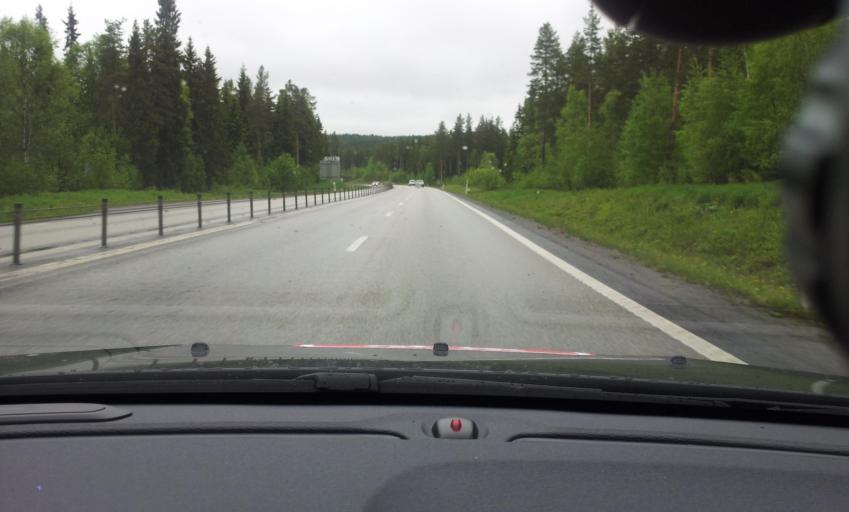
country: SE
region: Jaemtland
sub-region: OEstersunds Kommun
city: Ostersund
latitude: 63.1867
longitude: 14.6891
